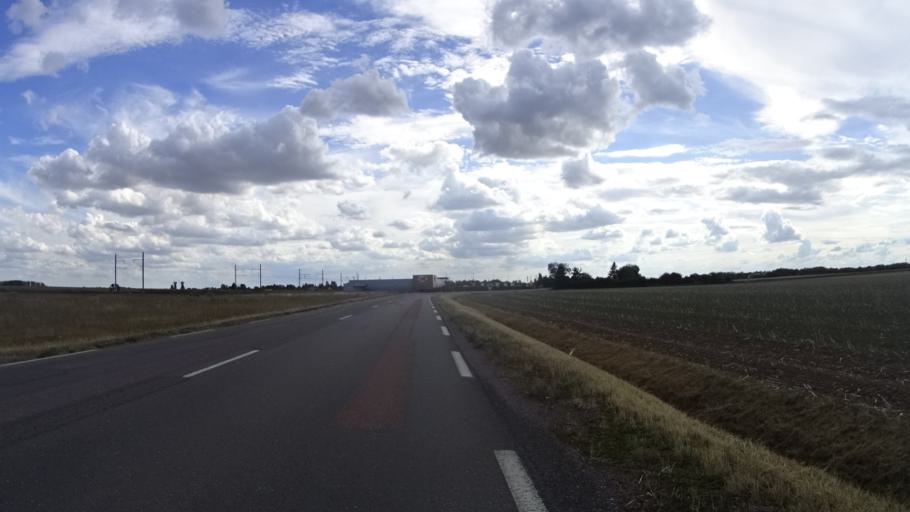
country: FR
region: Bourgogne
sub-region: Departement de la Cote-d'Or
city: Seurre
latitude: 47.0127
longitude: 5.1594
